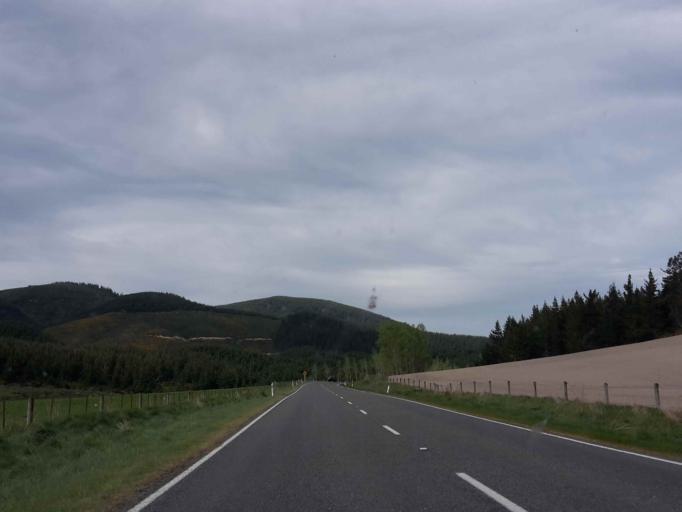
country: NZ
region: Canterbury
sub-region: Timaru District
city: Pleasant Point
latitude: -44.1206
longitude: 171.0527
